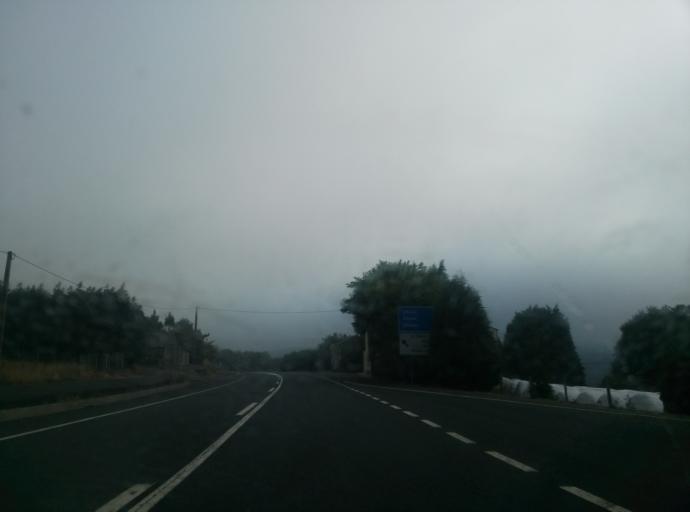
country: ES
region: Galicia
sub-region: Provincia de Lugo
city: Muras
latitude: 43.4679
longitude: -7.7019
